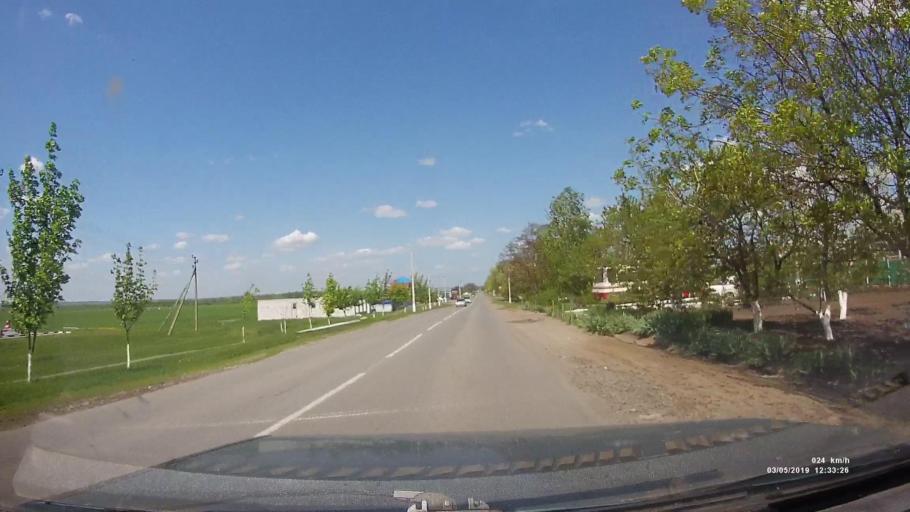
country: RU
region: Rostov
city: Semikarakorsk
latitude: 47.5131
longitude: 40.7717
